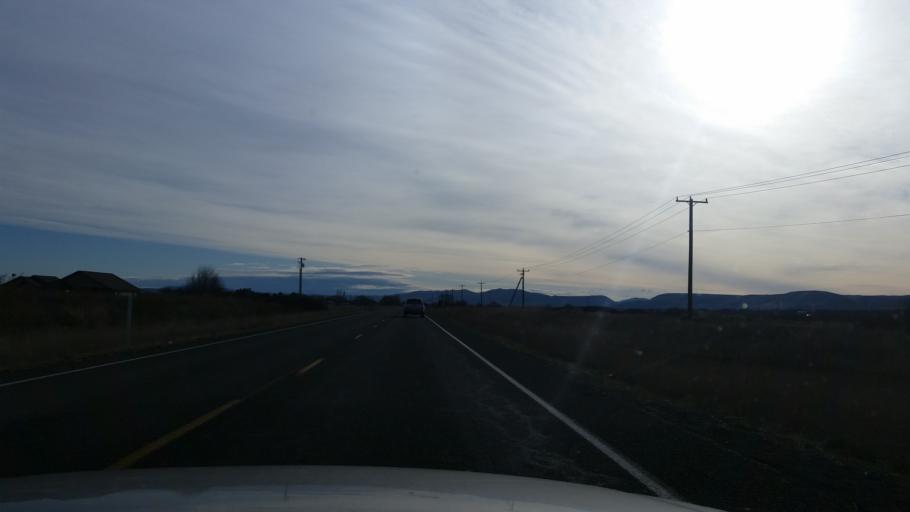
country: US
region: Washington
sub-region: Kittitas County
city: Ellensburg
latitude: 47.0322
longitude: -120.6075
